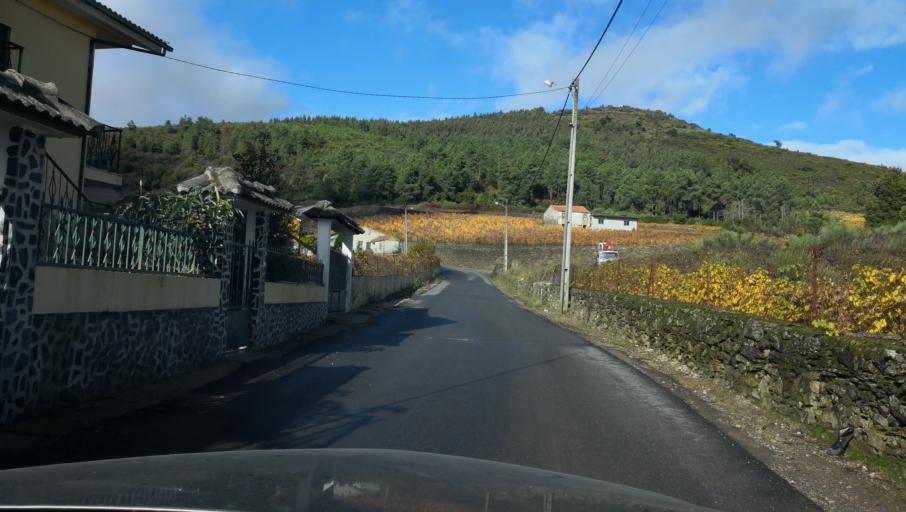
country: PT
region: Vila Real
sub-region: Sabrosa
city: Vilela
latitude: 41.2198
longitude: -7.5724
